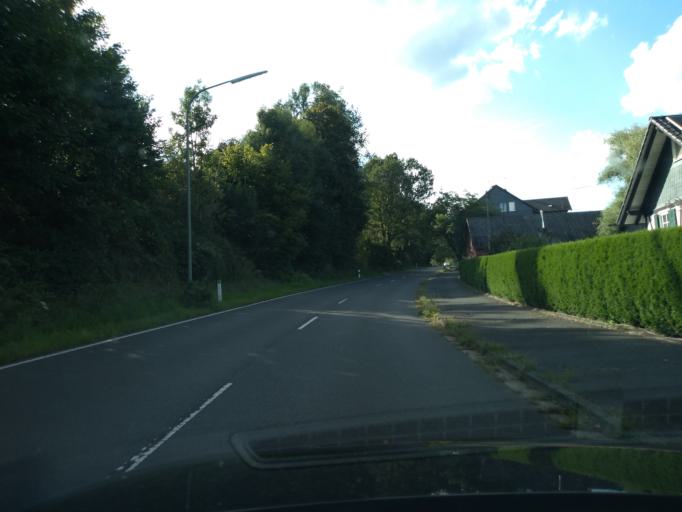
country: DE
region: North Rhine-Westphalia
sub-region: Regierungsbezirk Koln
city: Much
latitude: 50.8500
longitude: 7.3849
